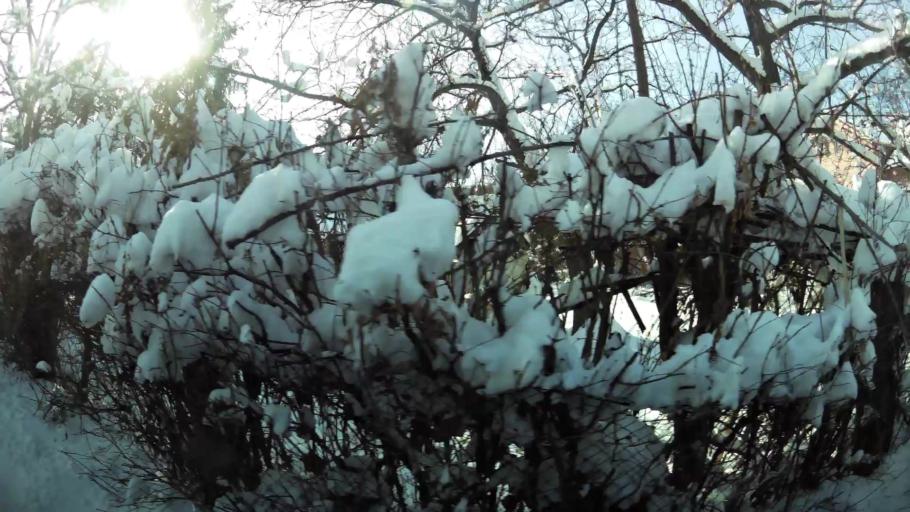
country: RS
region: Central Serbia
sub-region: Belgrade
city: Palilula
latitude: 44.7967
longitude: 20.5317
